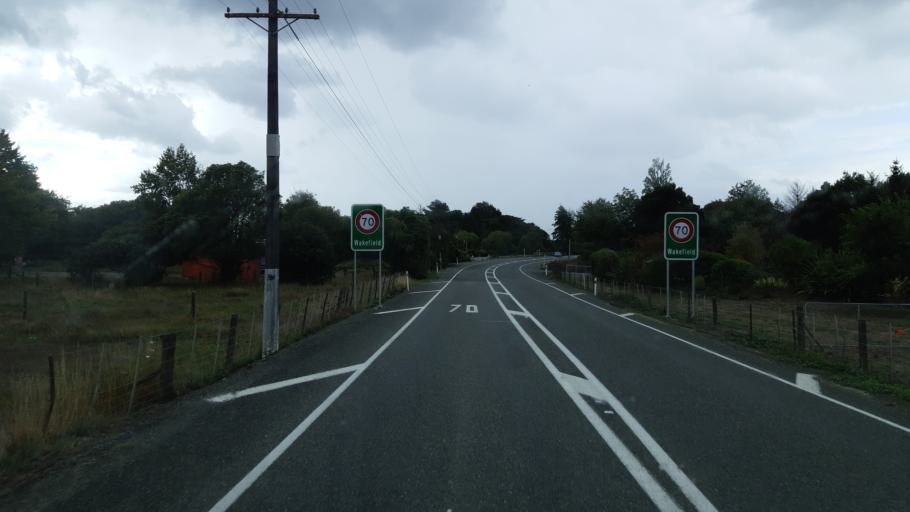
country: NZ
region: Tasman
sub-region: Tasman District
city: Wakefield
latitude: -41.4086
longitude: 173.0300
